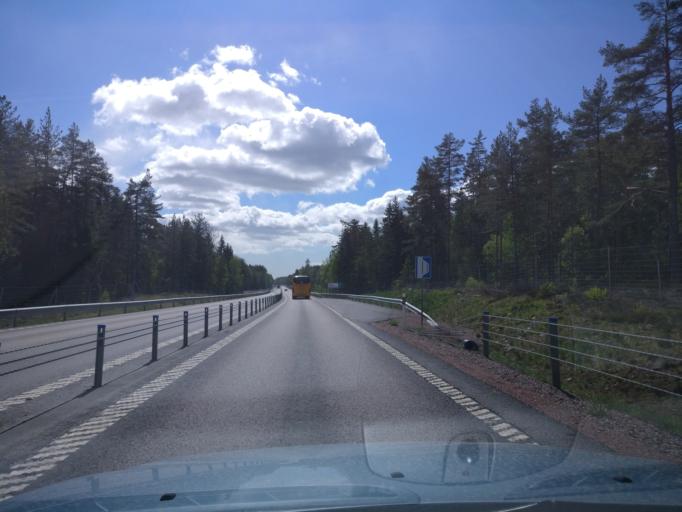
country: SE
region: Vaermland
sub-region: Karlstads Kommun
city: Karlstad
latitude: 59.4210
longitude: 13.5333
